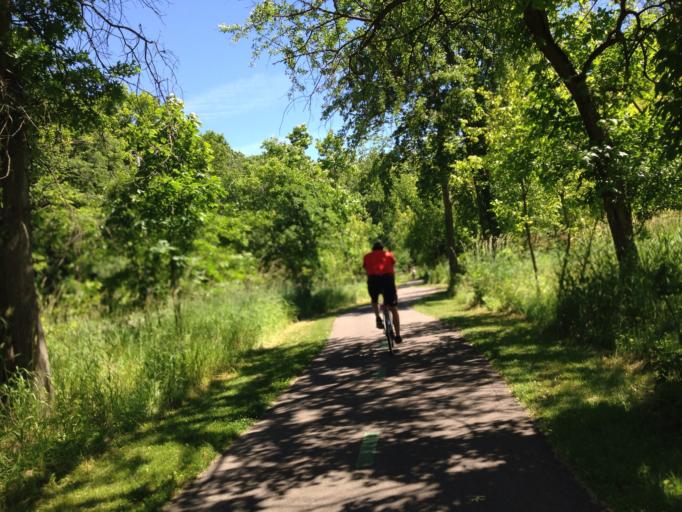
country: US
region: Ohio
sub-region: Cuyahoga County
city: Berea
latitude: 41.3499
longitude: -81.8434
